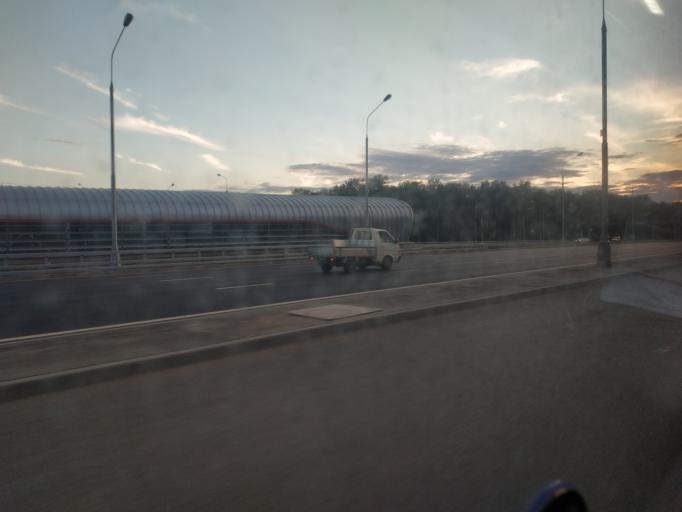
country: RU
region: Moscow
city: Solntsevo
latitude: 55.6031
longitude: 37.4056
